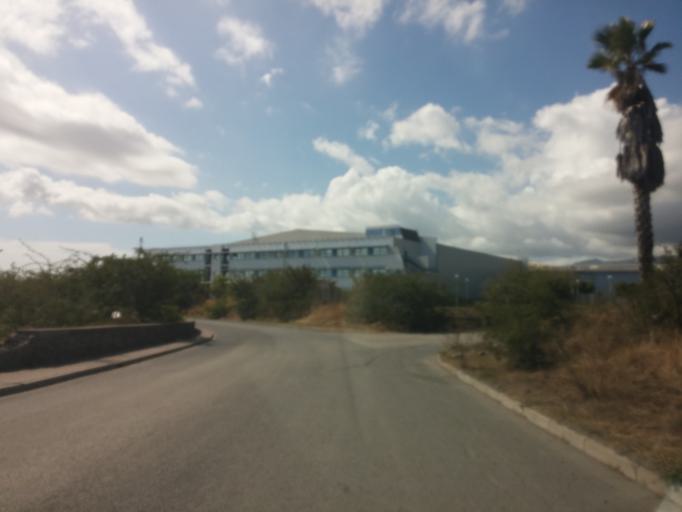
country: RE
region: Reunion
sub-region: Reunion
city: Le Port
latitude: -20.9451
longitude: 55.2833
